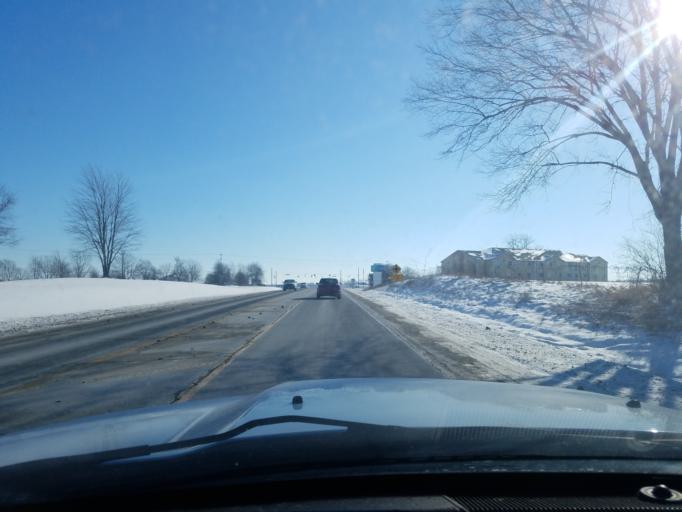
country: US
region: Indiana
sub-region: Noble County
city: Kendallville
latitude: 41.4466
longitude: -85.2344
